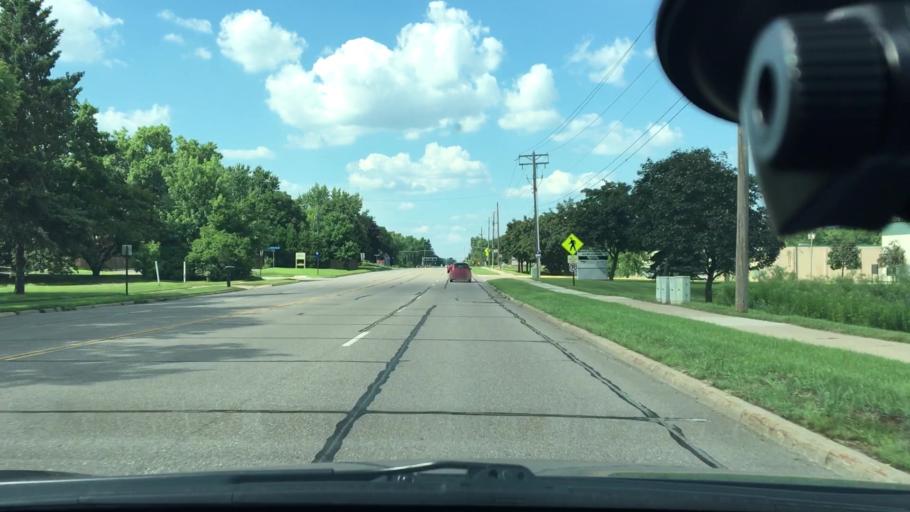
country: US
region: Minnesota
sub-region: Hennepin County
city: New Hope
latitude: 45.0452
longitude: -93.3803
